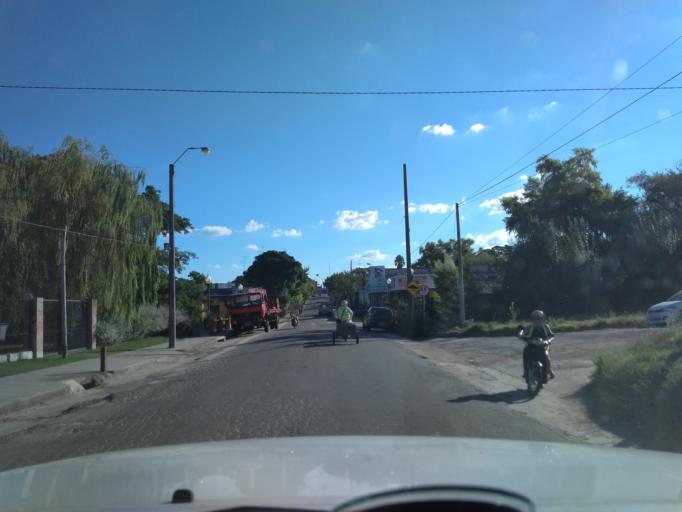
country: UY
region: Florida
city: Florida
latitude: -34.0967
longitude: -56.2243
